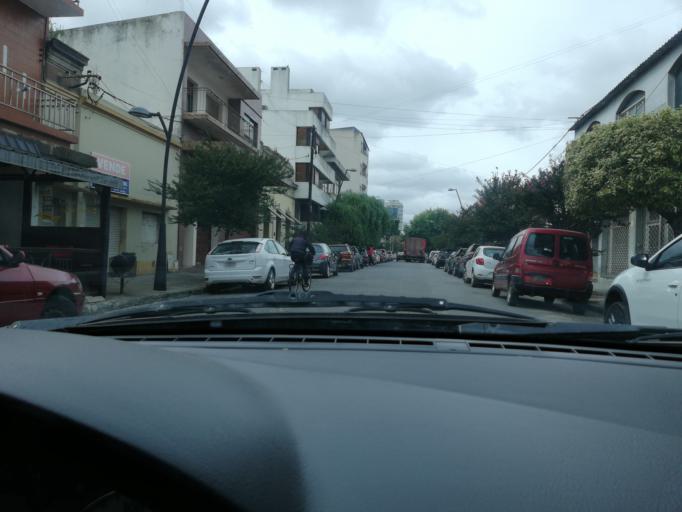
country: AR
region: Buenos Aires
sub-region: Partido de Balcarce
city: Balcarce
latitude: -37.8490
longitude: -58.2583
